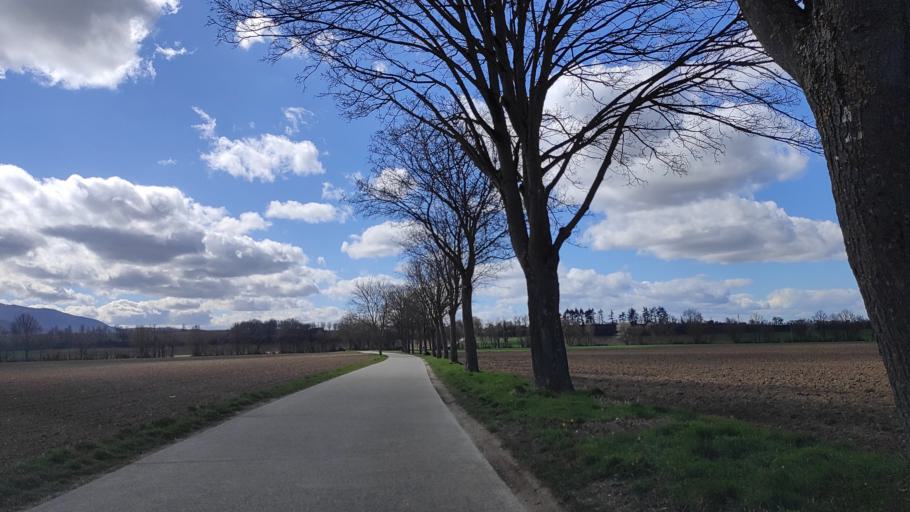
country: DE
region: Baden-Wuerttemberg
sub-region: Freiburg Region
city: Heitersheim
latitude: 47.8810
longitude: 7.6814
